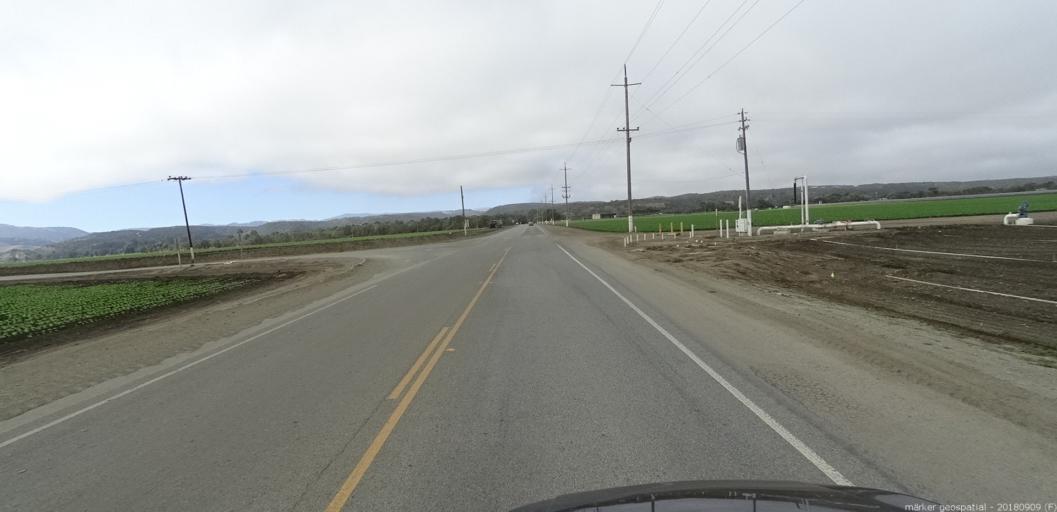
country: US
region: California
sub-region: Monterey County
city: Salinas
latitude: 36.6521
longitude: -121.6976
